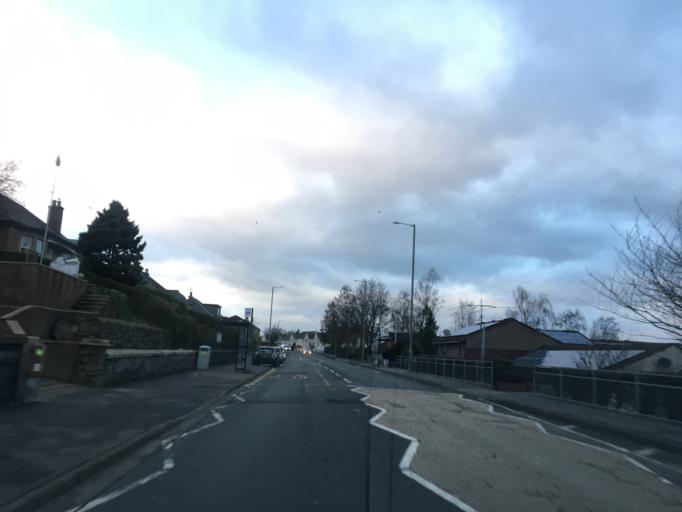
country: GB
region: Scotland
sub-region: Stirling
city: Bannockburn
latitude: 56.0980
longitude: -3.9281
